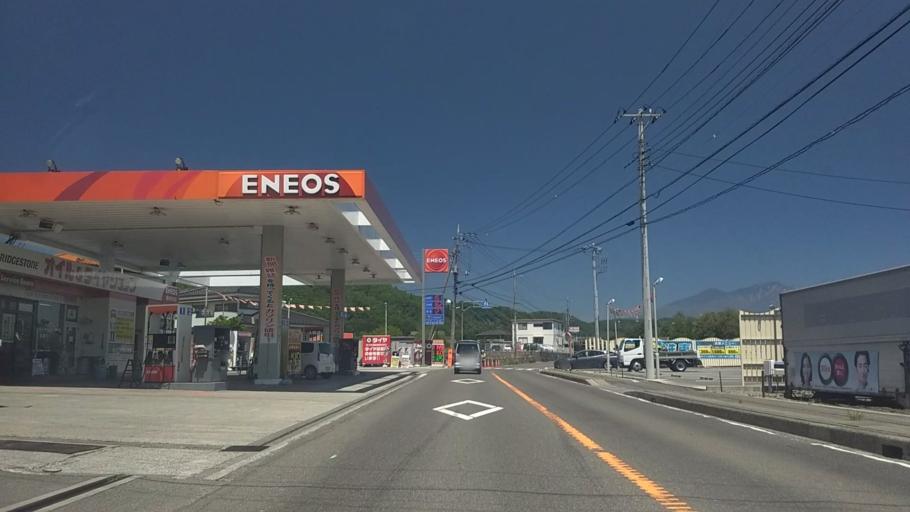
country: JP
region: Yamanashi
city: Nirasaki
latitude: 35.7622
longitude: 138.4294
